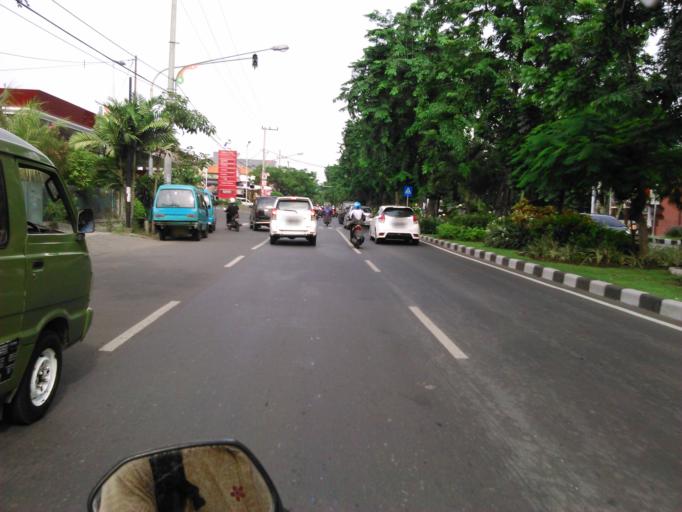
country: ID
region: East Java
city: Brongkalan
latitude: -7.2667
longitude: 112.7689
